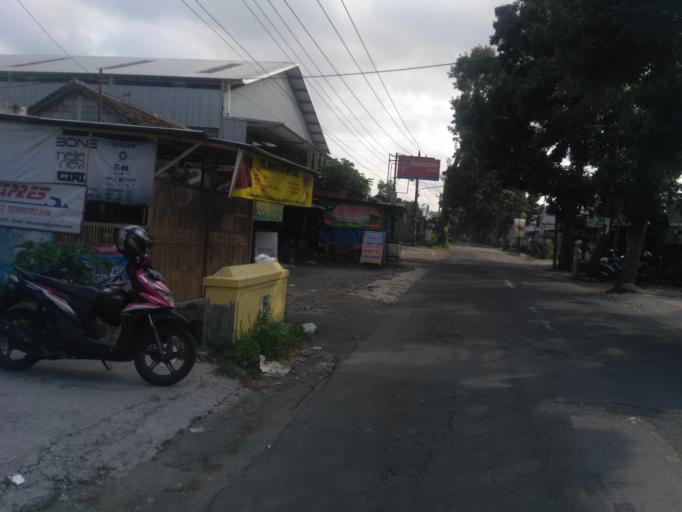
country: ID
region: Daerah Istimewa Yogyakarta
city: Yogyakarta
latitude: -7.7776
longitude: 110.3414
